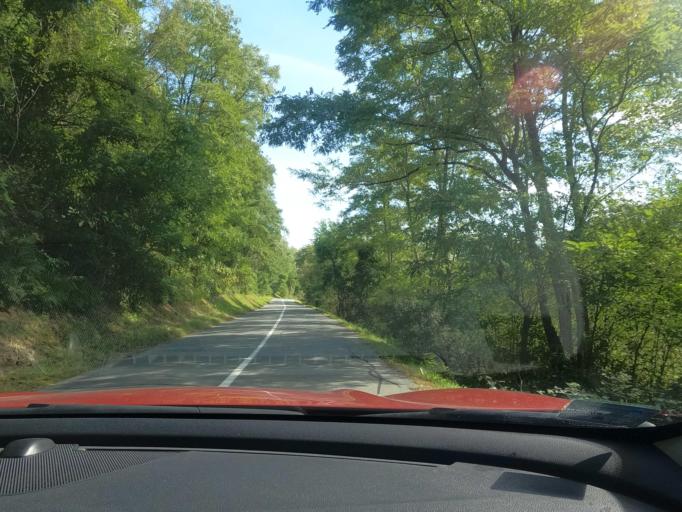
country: HR
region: Sisacko-Moslavacka
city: Petrinja
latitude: 45.3832
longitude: 16.2935
